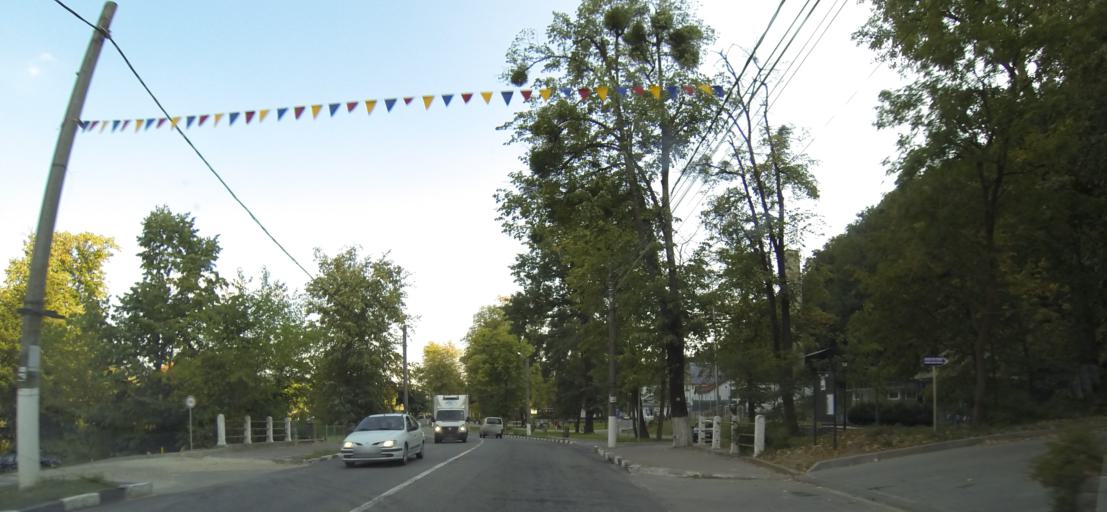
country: RO
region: Valcea
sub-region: Oras Calimanesti
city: Jiblea Veche
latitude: 45.2498
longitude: 24.3371
